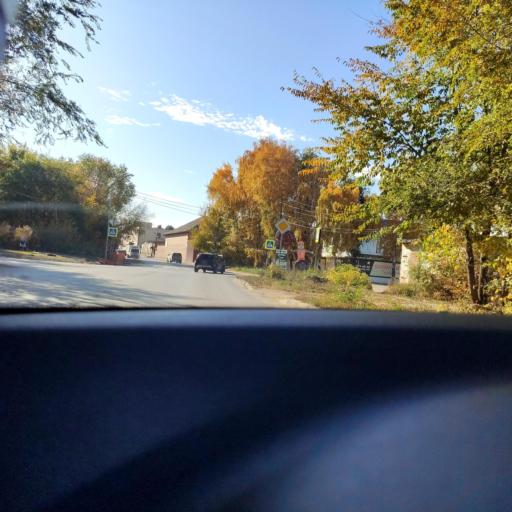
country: RU
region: Samara
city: Petra-Dubrava
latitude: 53.2368
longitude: 50.2947
